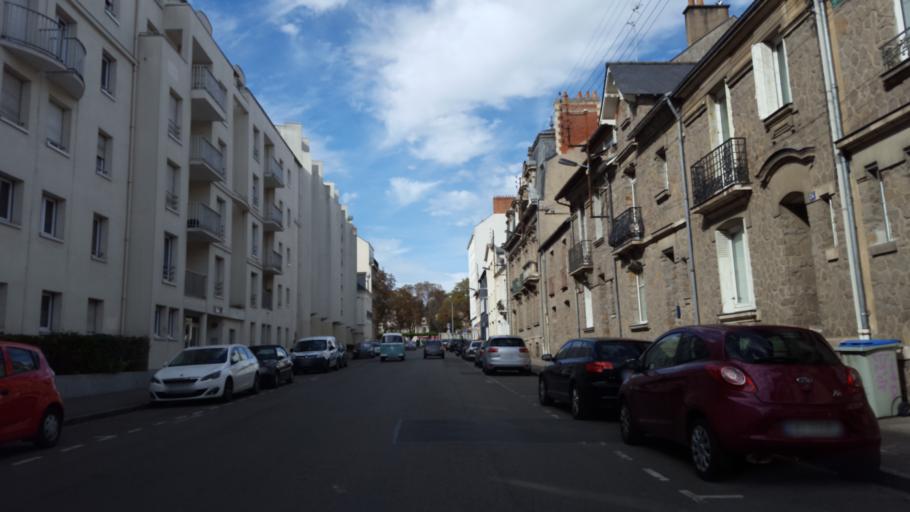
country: FR
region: Pays de la Loire
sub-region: Departement de la Loire-Atlantique
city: Nantes
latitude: 47.2134
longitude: -1.5730
